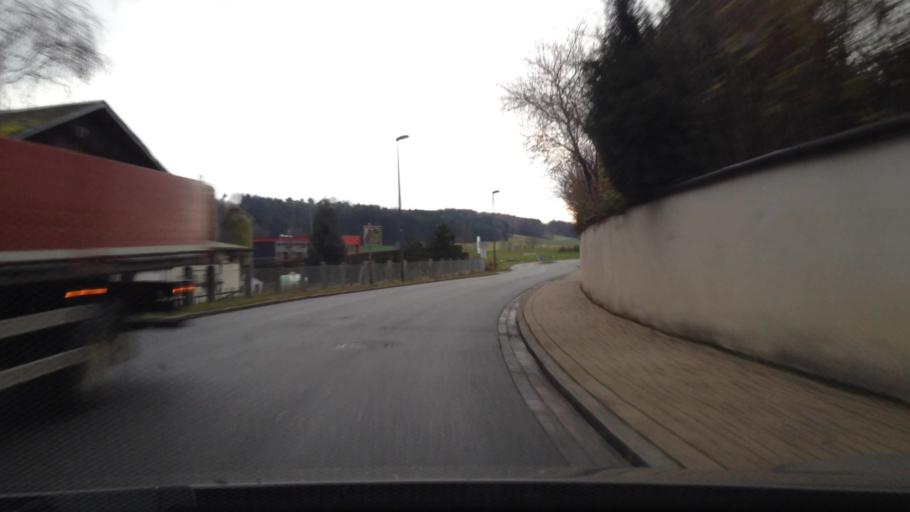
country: DE
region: Bavaria
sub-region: Regierungsbezirk Mittelfranken
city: Burghaslach
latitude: 49.7334
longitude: 10.5964
